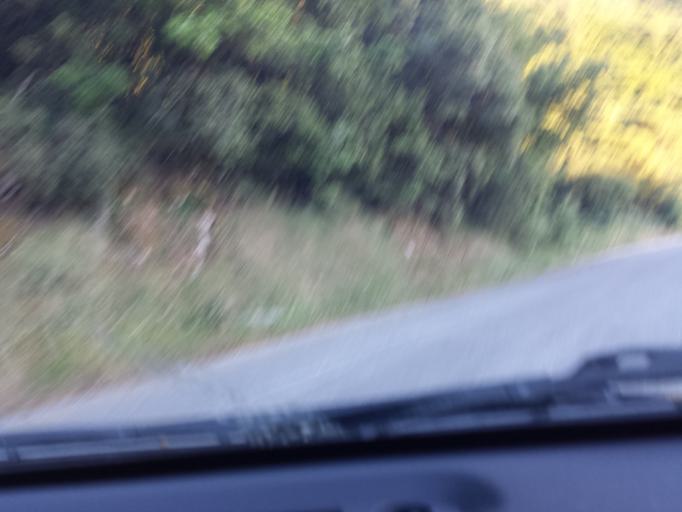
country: GR
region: Ionian Islands
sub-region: Nomos Kerkyras
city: Acharavi
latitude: 39.7362
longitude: 19.8394
